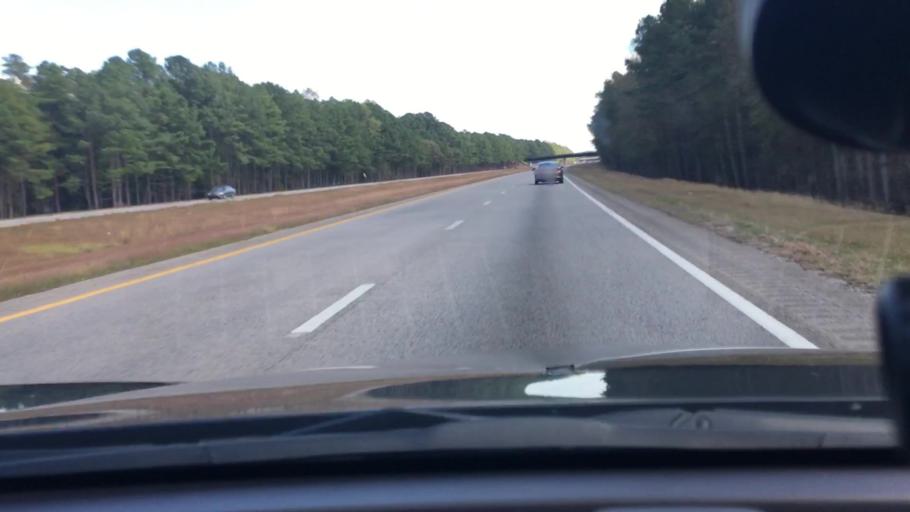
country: US
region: North Carolina
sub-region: Nash County
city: Spring Hope
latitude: 35.7845
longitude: -78.0954
